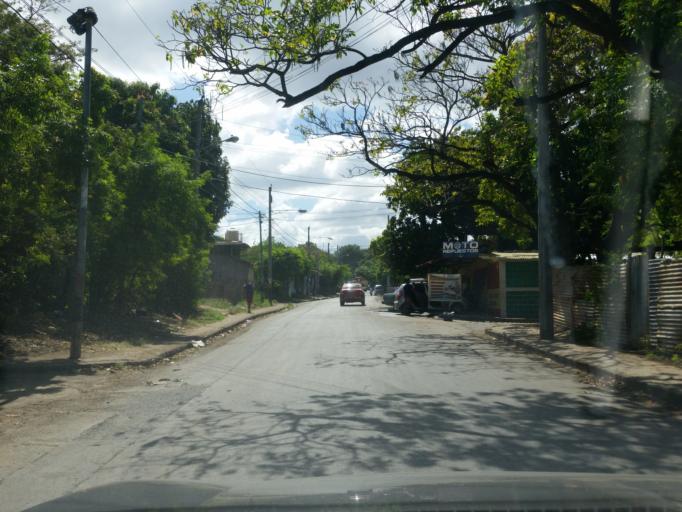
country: NI
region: Managua
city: Managua
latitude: 12.1177
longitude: -86.2322
